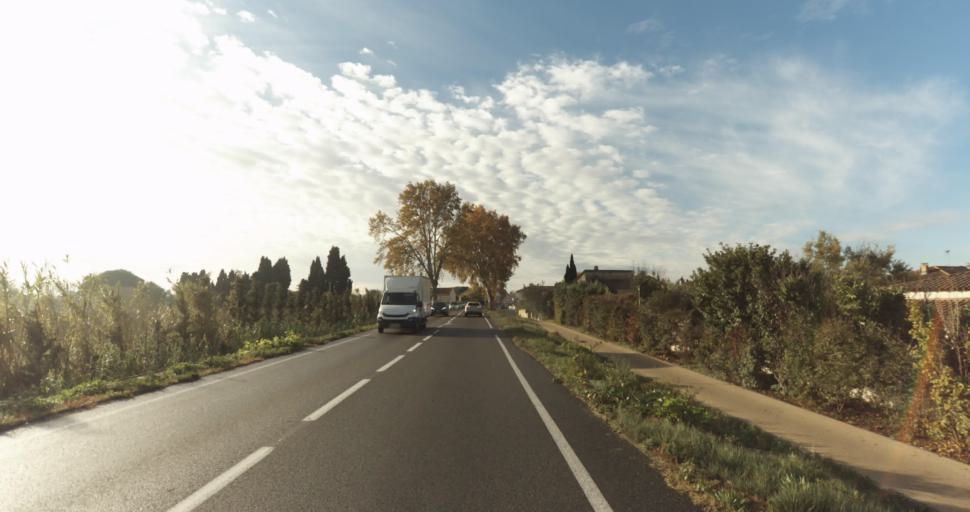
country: FR
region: Provence-Alpes-Cote d'Azur
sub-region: Departement des Bouches-du-Rhone
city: Rognonas
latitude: 43.9078
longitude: 4.8049
